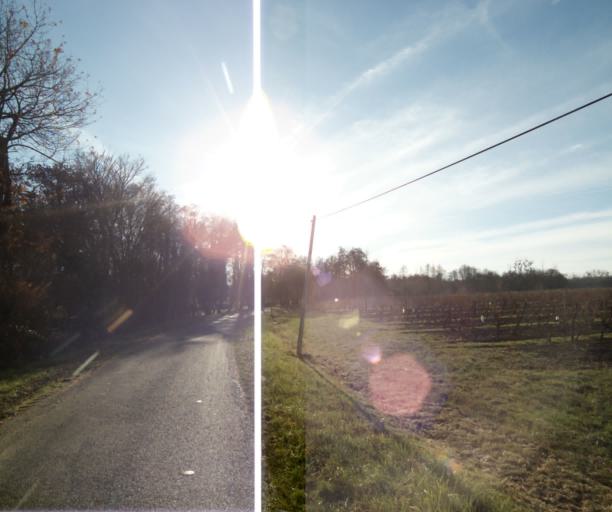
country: FR
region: Poitou-Charentes
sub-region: Departement de la Charente-Maritime
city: Burie
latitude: 45.7898
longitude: -0.4180
